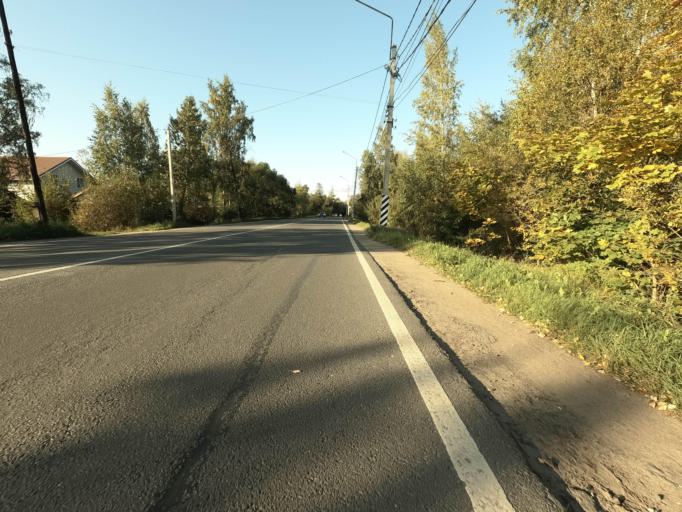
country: RU
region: St.-Petersburg
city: Kolpino
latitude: 59.7533
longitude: 30.6158
